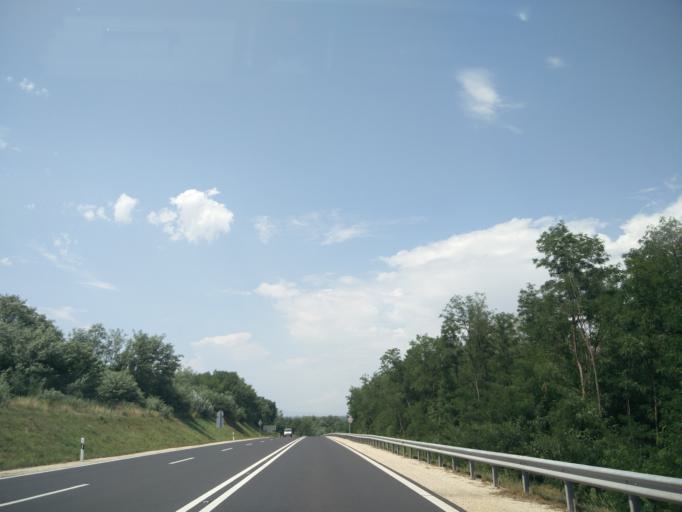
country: HU
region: Vas
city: Vasvar
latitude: 47.0986
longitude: 16.8919
